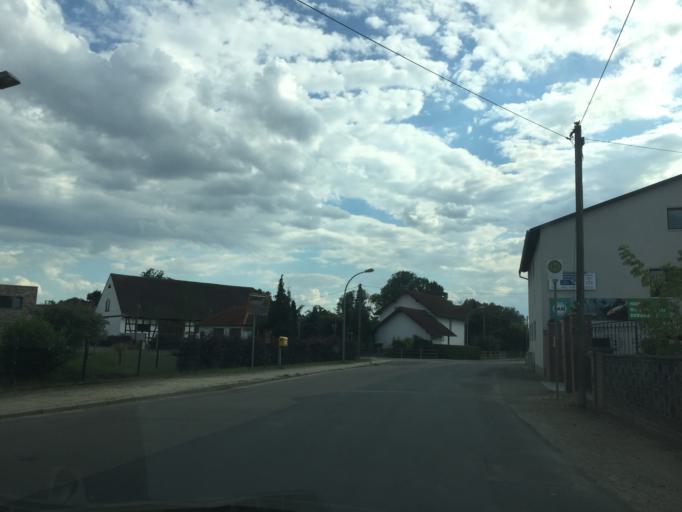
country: DE
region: Thuringia
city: Saara
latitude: 50.9519
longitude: 12.4298
